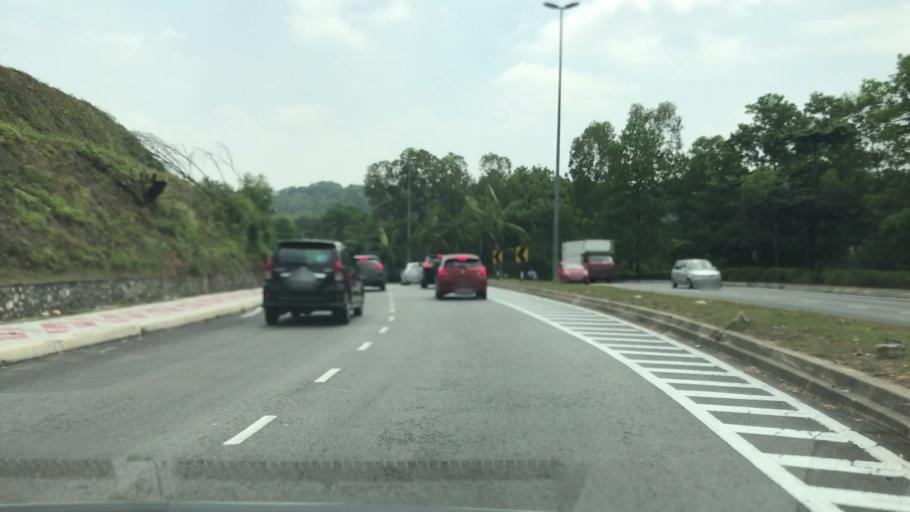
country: MY
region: Selangor
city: Kampong Baharu Balakong
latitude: 3.0289
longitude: 101.6807
